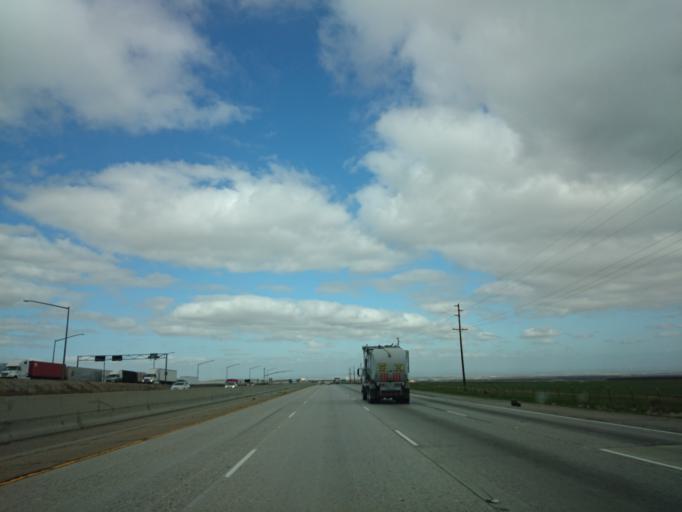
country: US
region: California
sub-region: Kern County
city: Frazier Park
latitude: 34.9605
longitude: -118.9370
